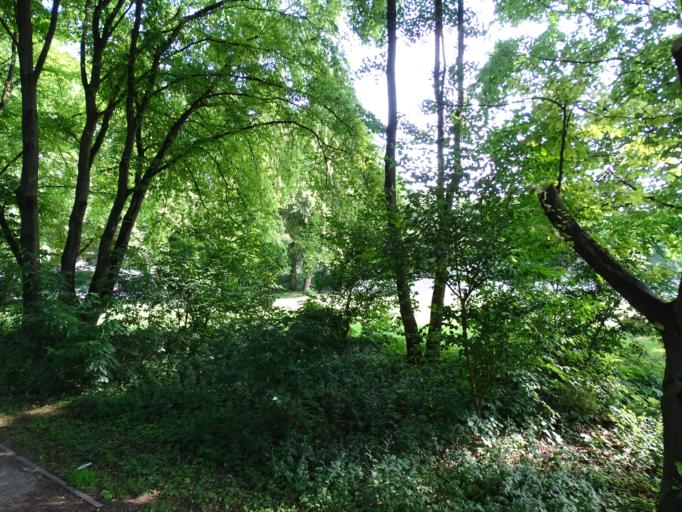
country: DE
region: Bavaria
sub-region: Upper Bavaria
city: Oberschleissheim
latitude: 48.2163
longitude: 11.5549
